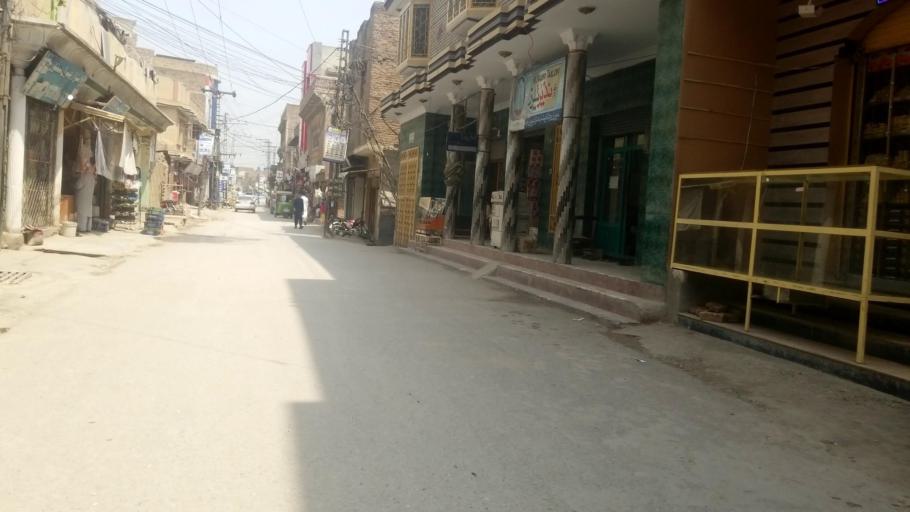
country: PK
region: Khyber Pakhtunkhwa
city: Peshawar
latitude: 34.0310
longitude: 71.5857
